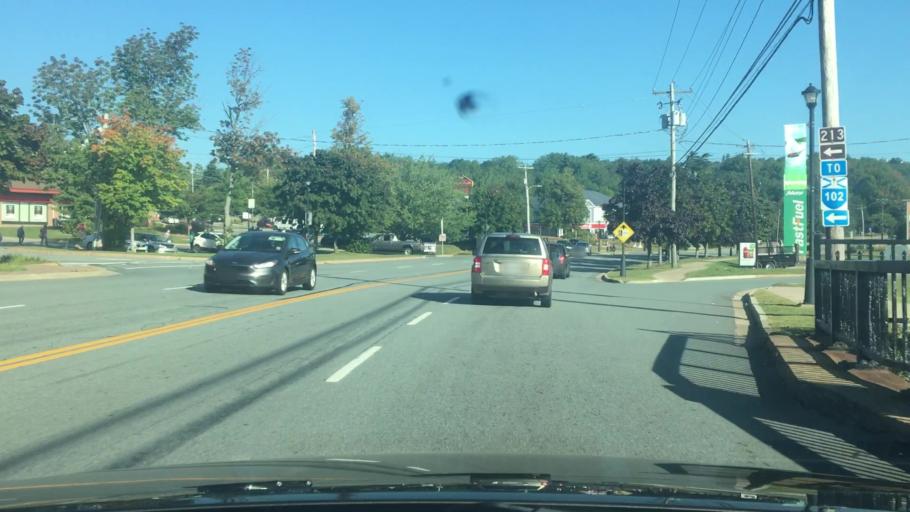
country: CA
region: Nova Scotia
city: Dartmouth
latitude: 44.7140
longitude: -63.6777
